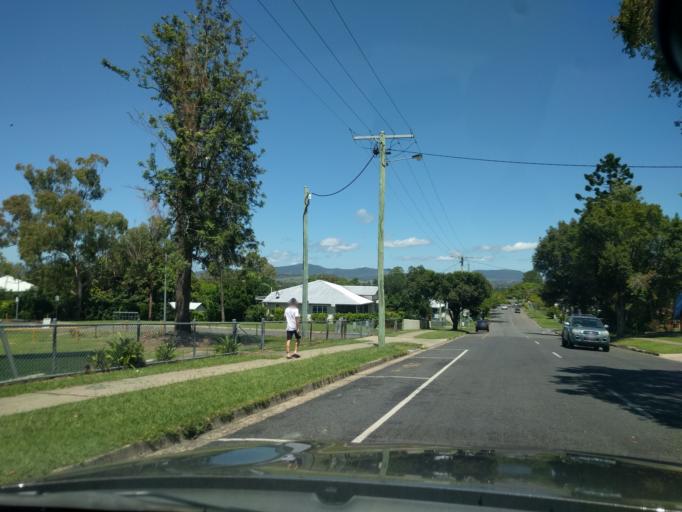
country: AU
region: Queensland
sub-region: Logan
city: Cedar Vale
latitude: -27.9876
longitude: 153.0035
